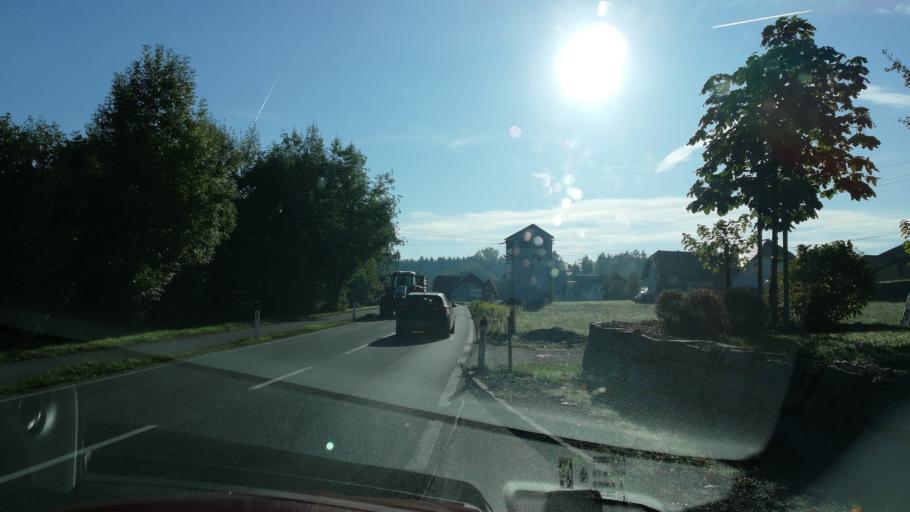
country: AT
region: Upper Austria
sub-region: Politischer Bezirk Steyr-Land
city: Waldneukirchen
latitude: 48.0186
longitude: 14.2351
